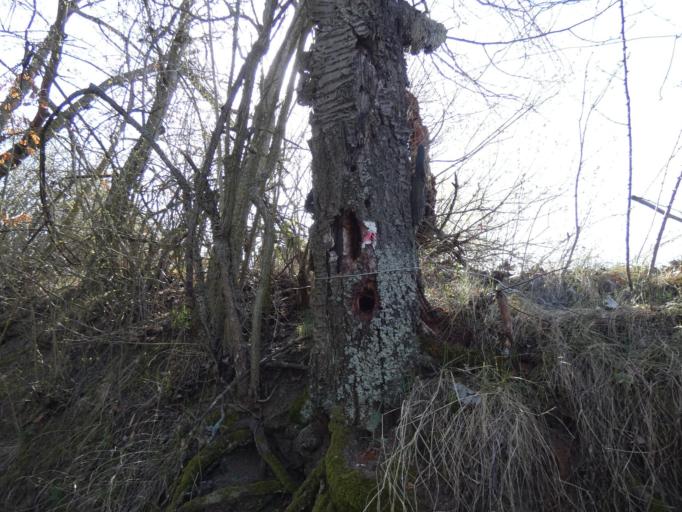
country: HU
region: Pest
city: Szob
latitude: 47.8666
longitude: 18.8835
